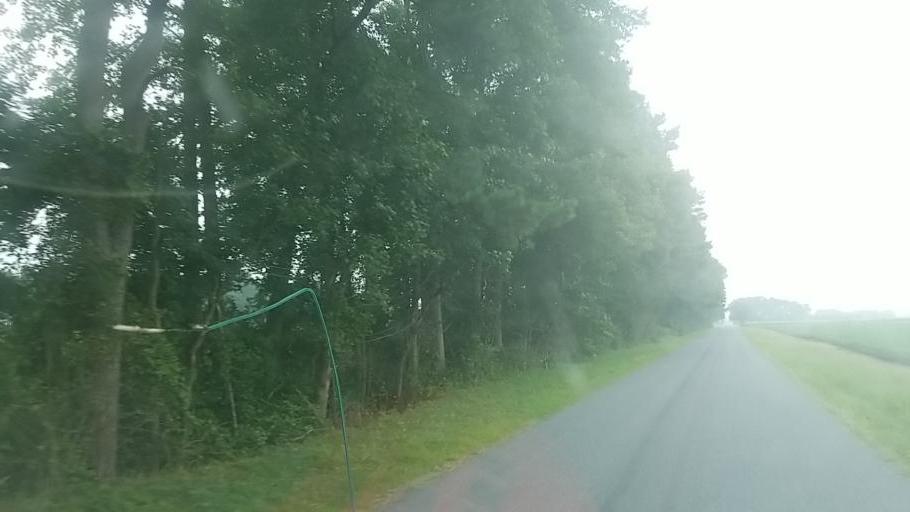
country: US
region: Maryland
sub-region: Wicomico County
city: Pittsville
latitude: 38.4522
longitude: -75.3761
